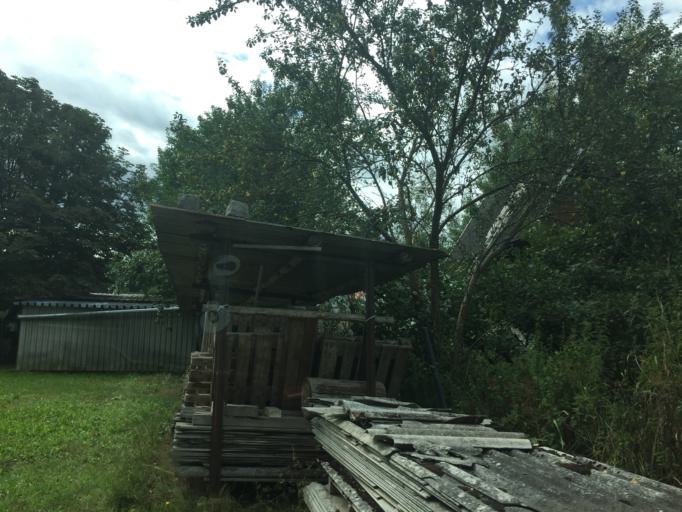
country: DE
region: Bavaria
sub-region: Upper Palatinate
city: Pressath
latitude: 49.7648
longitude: 11.9284
